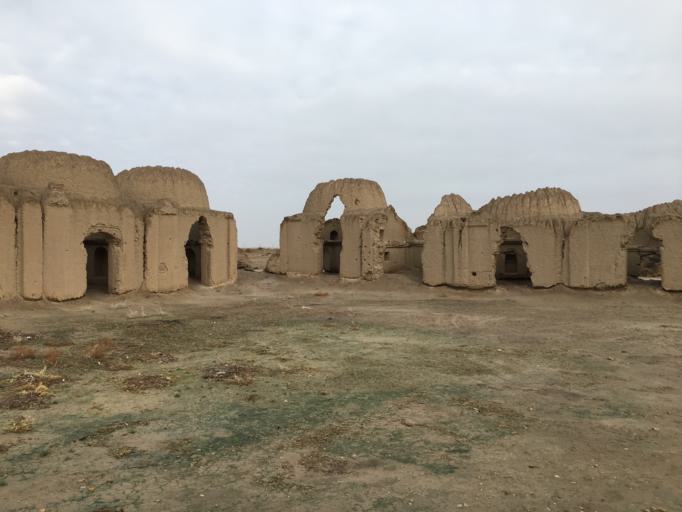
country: TM
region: Mary
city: Bayramaly
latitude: 37.4117
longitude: 62.1688
